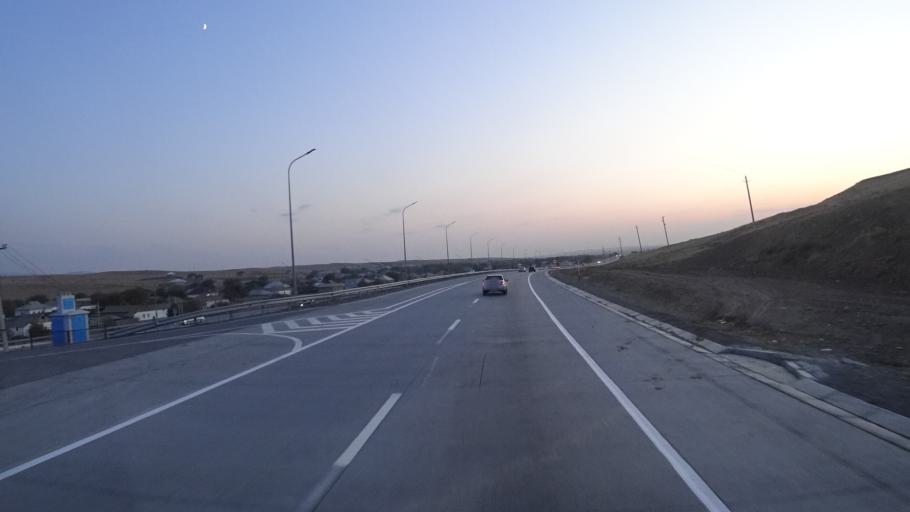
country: KZ
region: Ongtustik Qazaqstan
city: Qazyqurt
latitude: 41.8971
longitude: 69.4535
